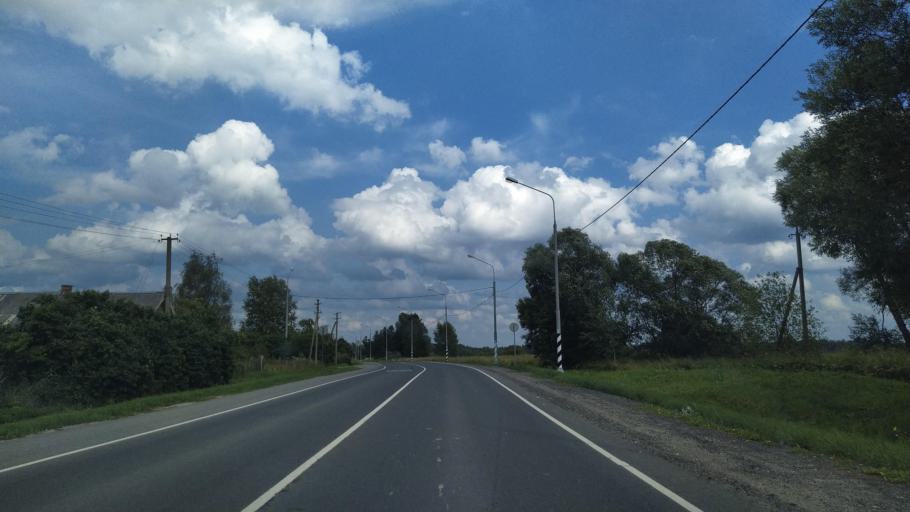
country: RU
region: Pskov
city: Dno
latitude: 58.0614
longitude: 30.0185
